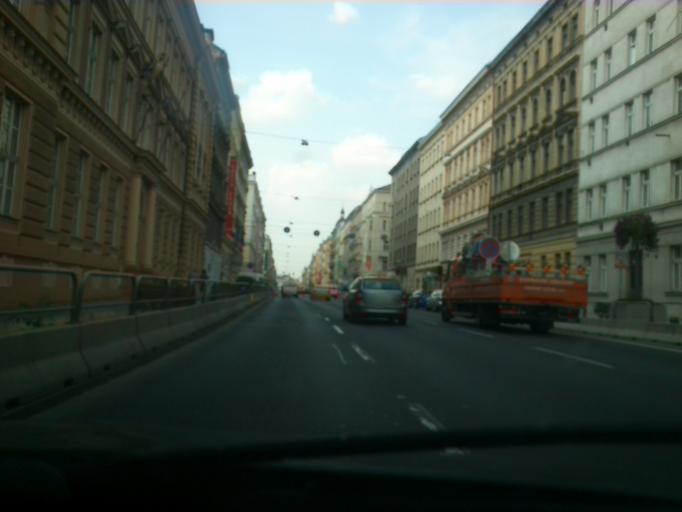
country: CZ
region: Praha
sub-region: Praha 2
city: Vysehrad
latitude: 50.0696
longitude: 14.4309
